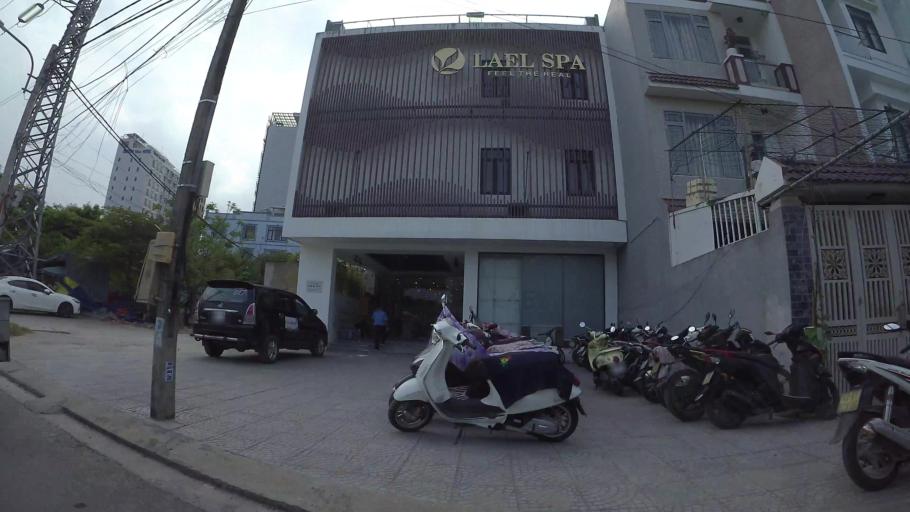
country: VN
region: Da Nang
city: Son Tra
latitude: 16.0626
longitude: 108.2386
